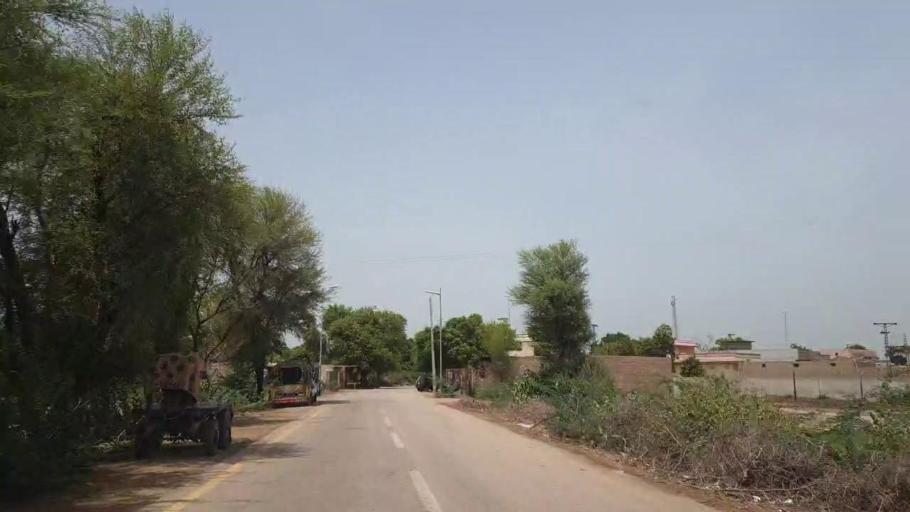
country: PK
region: Sindh
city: Sakrand
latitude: 26.2029
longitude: 68.2438
